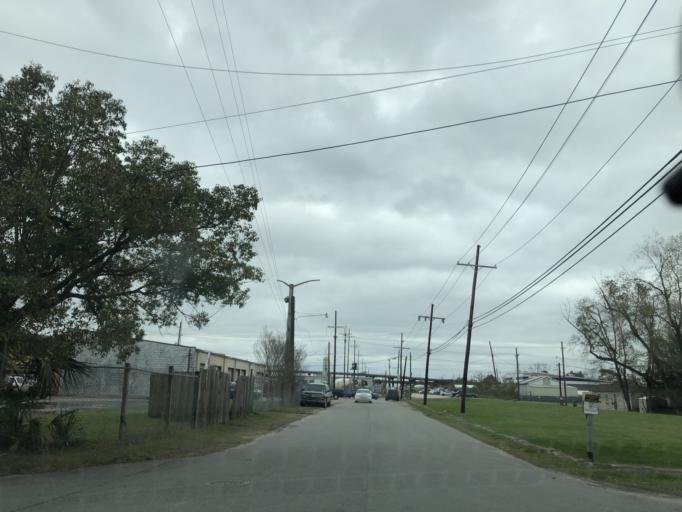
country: US
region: Louisiana
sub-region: Jefferson Parish
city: Metairie Terrace
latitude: 29.9743
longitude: -90.1620
